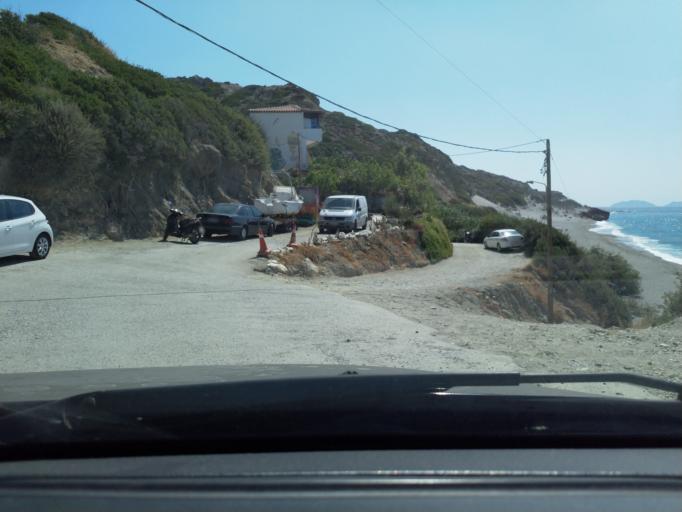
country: GR
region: Crete
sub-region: Nomos Rethymnis
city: Agia Foteini
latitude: 35.1382
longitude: 24.5296
